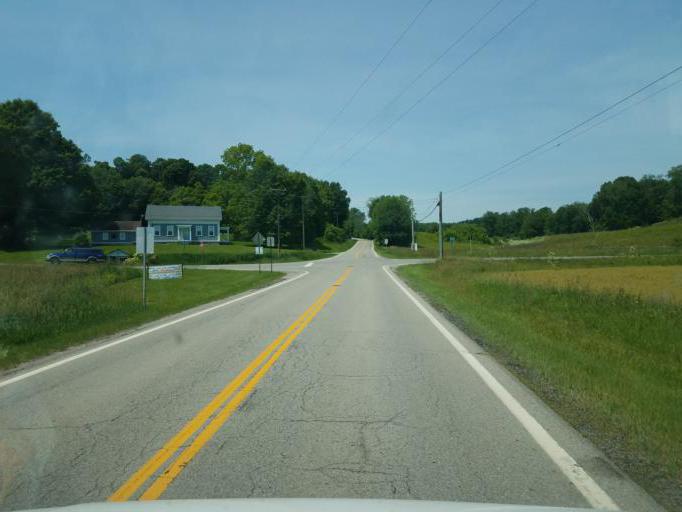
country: US
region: Ohio
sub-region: Ashland County
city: Loudonville
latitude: 40.6778
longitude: -82.2879
